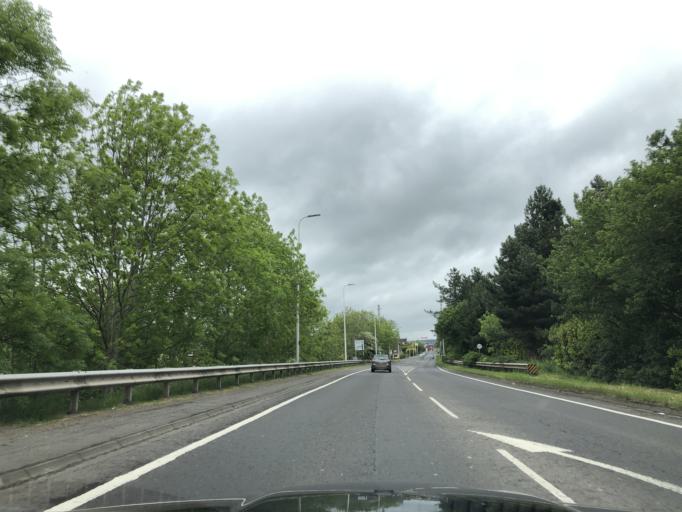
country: GB
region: Northern Ireland
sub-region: Lisburn District
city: Lisburn
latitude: 54.5233
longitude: -6.0742
